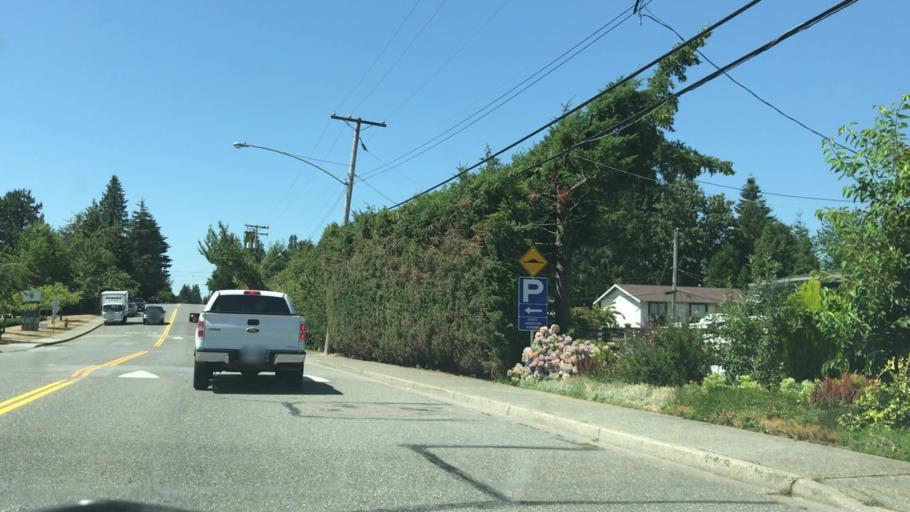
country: CA
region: British Columbia
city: Aldergrove
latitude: 49.0556
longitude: -122.4817
